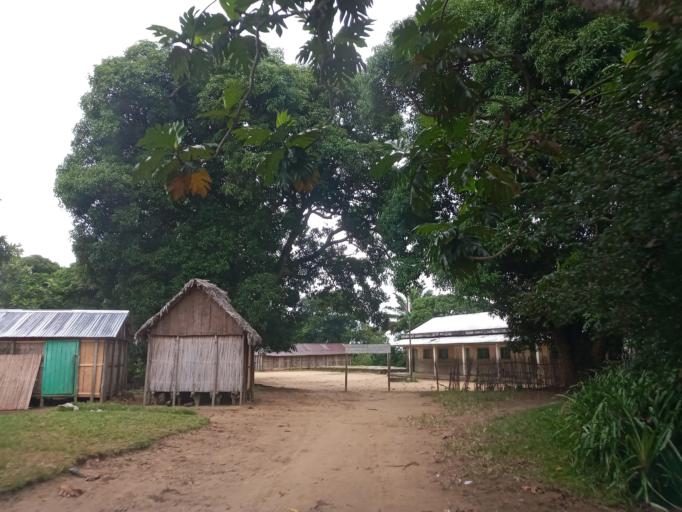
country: MG
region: Atsimo-Atsinanana
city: Vohipaho
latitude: -24.0441
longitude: 47.4393
